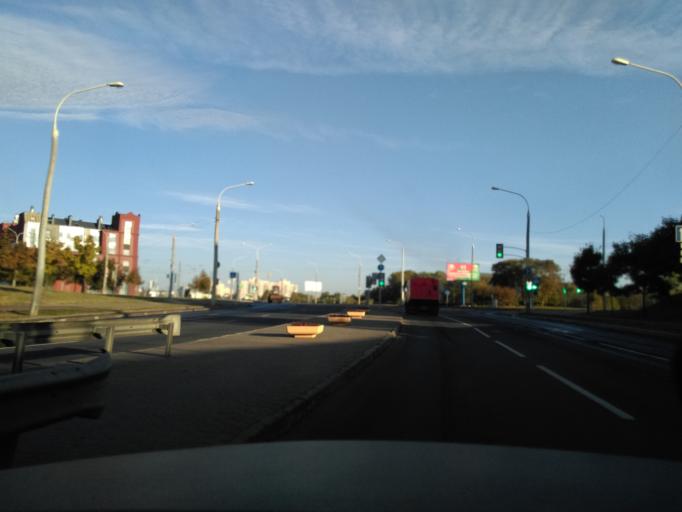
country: BY
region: Minsk
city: Minsk
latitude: 53.8885
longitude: 27.5797
